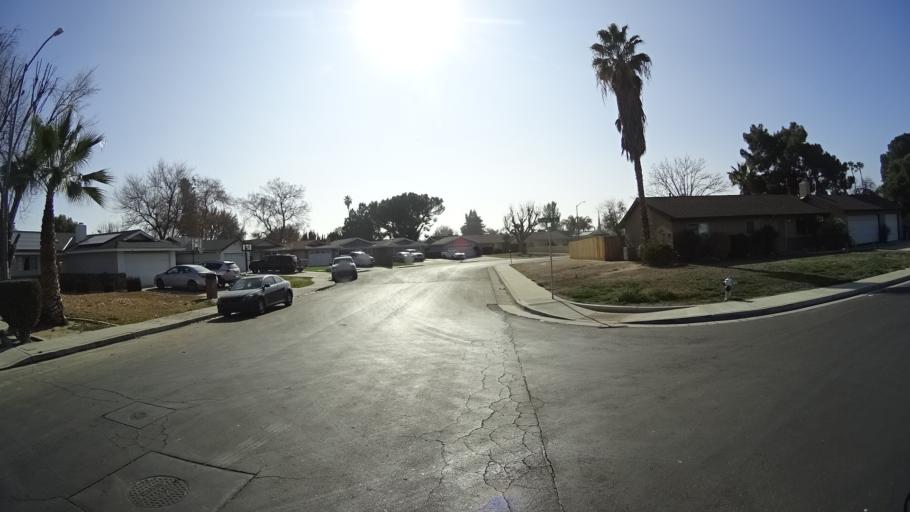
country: US
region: California
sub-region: Kern County
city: Bakersfield
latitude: 35.3296
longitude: -119.0587
